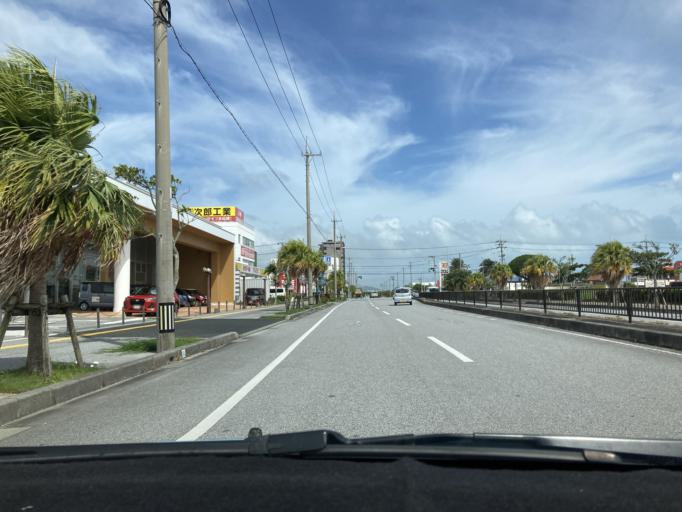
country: JP
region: Okinawa
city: Ginowan
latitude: 26.2047
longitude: 127.7615
